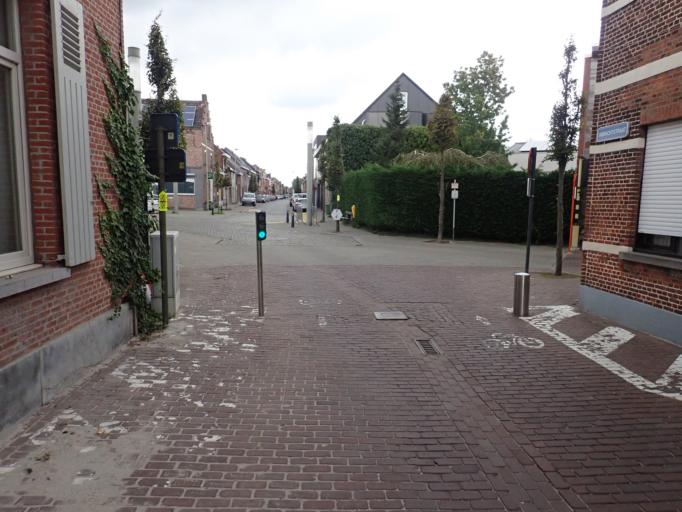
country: BE
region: Flanders
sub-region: Provincie Oost-Vlaanderen
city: Kruibeke
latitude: 51.1728
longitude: 4.3116
